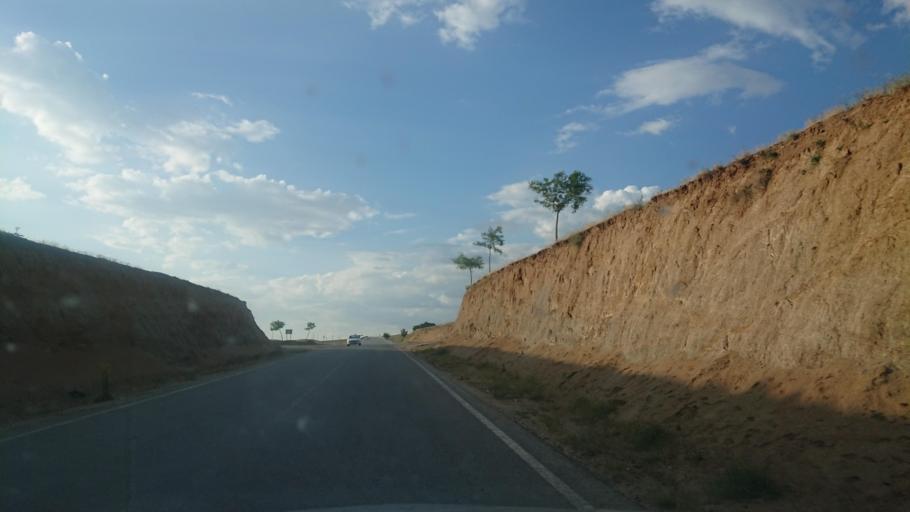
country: TR
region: Aksaray
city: Balci
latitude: 38.5915
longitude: 34.1020
